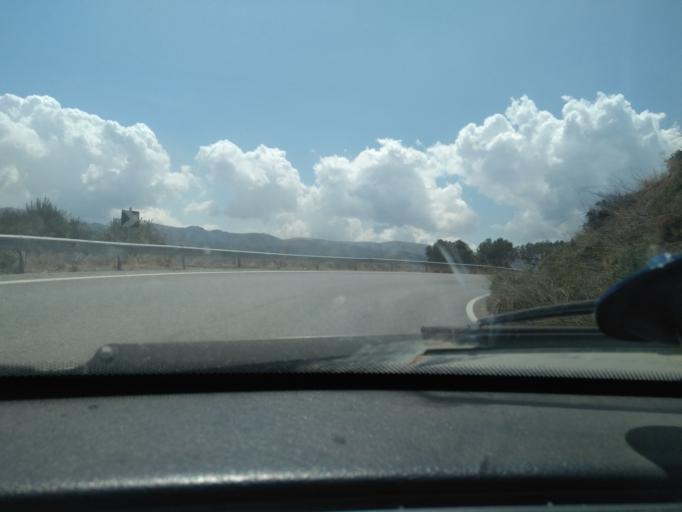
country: GR
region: Crete
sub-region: Nomos Lasithiou
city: Siteia
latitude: 35.1392
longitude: 26.0762
